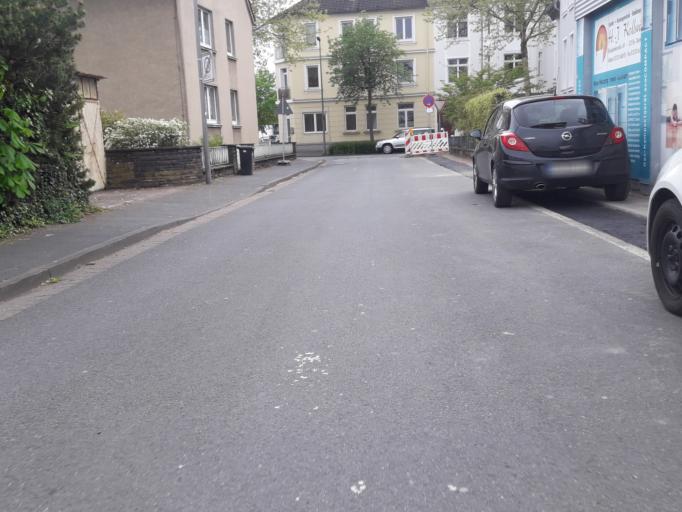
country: DE
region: North Rhine-Westphalia
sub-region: Regierungsbezirk Detmold
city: Detmold
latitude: 51.9406
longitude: 8.8672
